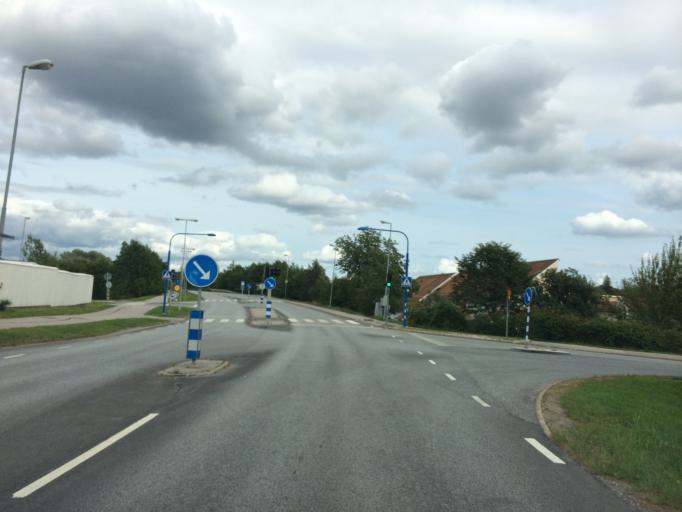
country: SE
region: Stockholm
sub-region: Sollentuna Kommun
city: Sollentuna
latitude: 59.4582
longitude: 17.9087
